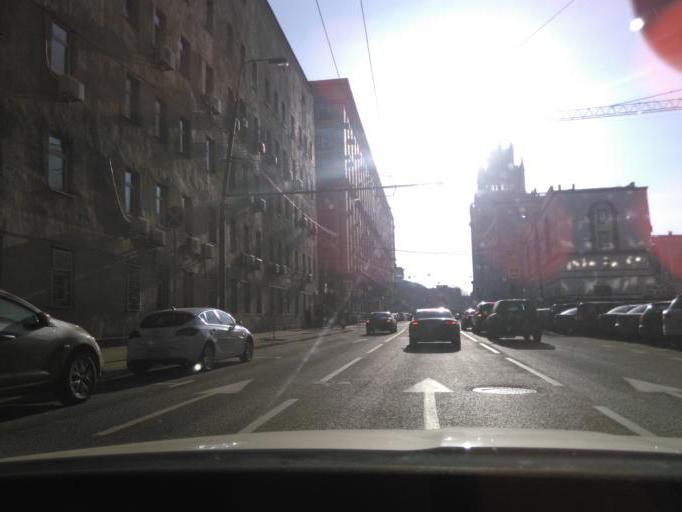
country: RU
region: Moscow
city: Moscow
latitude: 55.7705
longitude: 37.5915
